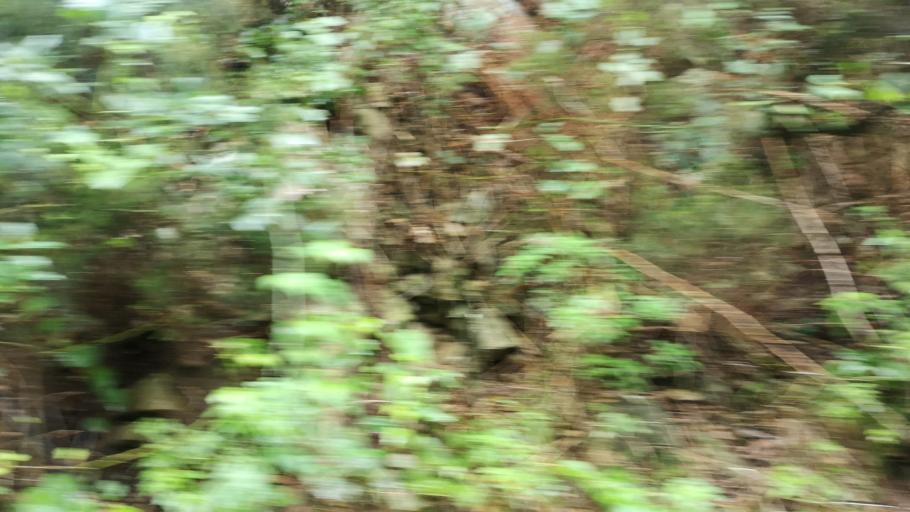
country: ES
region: Canary Islands
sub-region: Provincia de Santa Cruz de Tenerife
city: Vallehermosa
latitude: 28.1627
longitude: -17.2949
